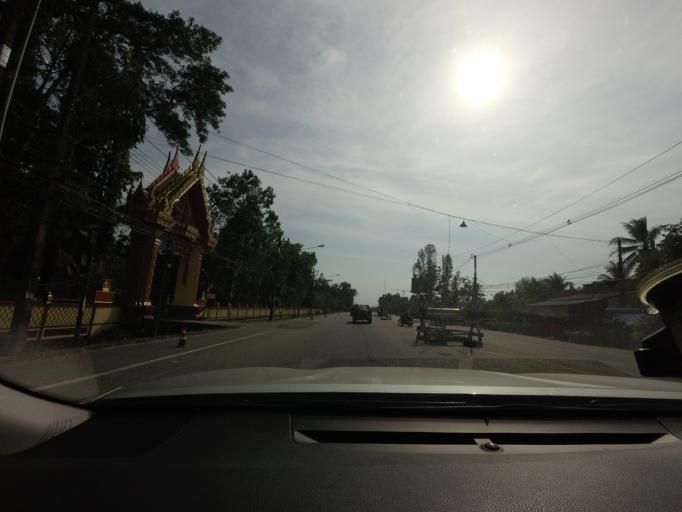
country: TH
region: Narathiwat
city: Narathiwat
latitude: 6.3790
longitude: 101.8017
